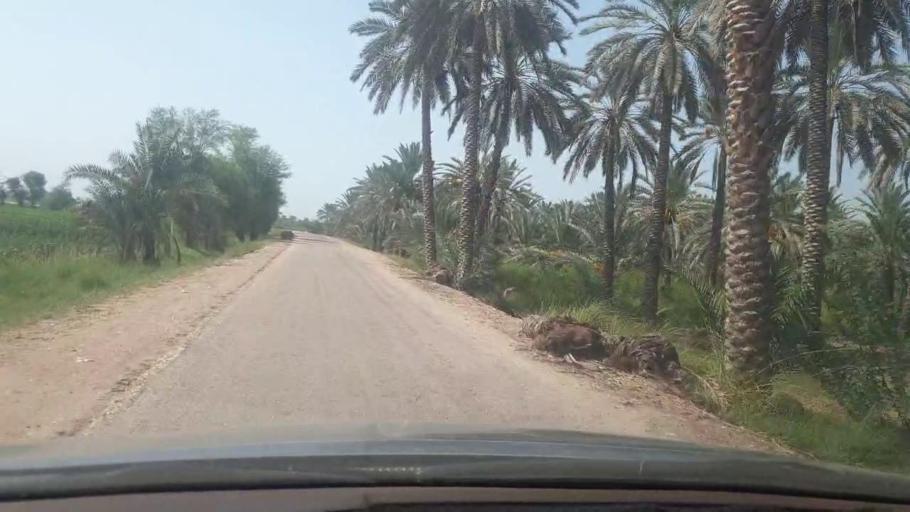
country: PK
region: Sindh
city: Ranipur
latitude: 27.2660
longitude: 68.5817
